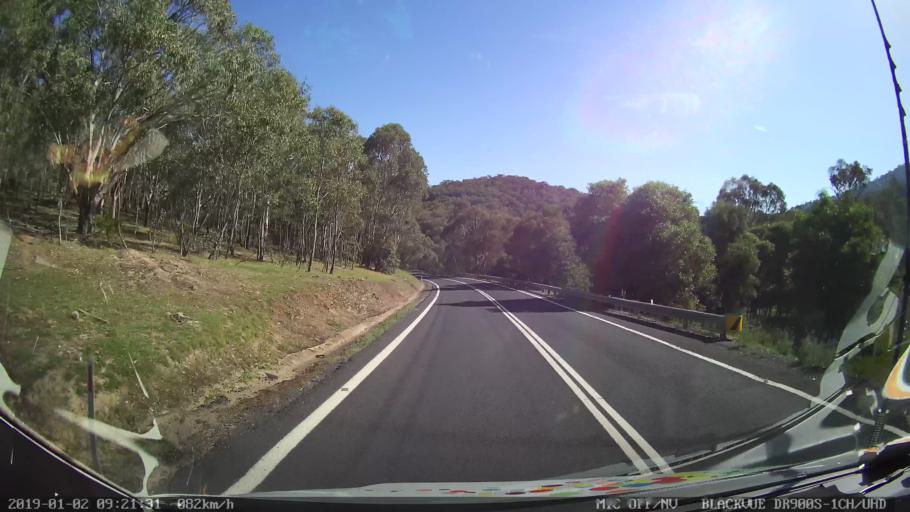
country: AU
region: New South Wales
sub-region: Tumut Shire
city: Tumut
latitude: -35.4049
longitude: 148.2915
